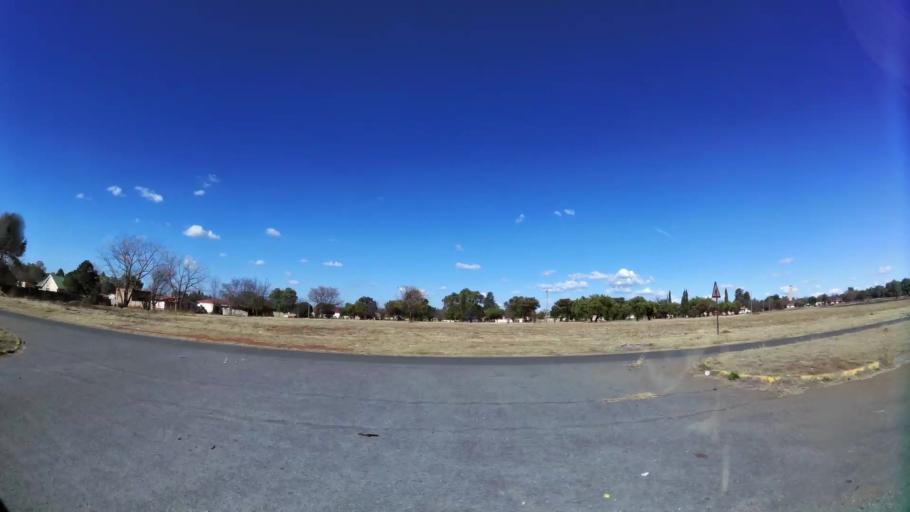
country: ZA
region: Gauteng
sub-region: West Rand District Municipality
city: Carletonville
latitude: -26.3664
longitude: 27.3780
